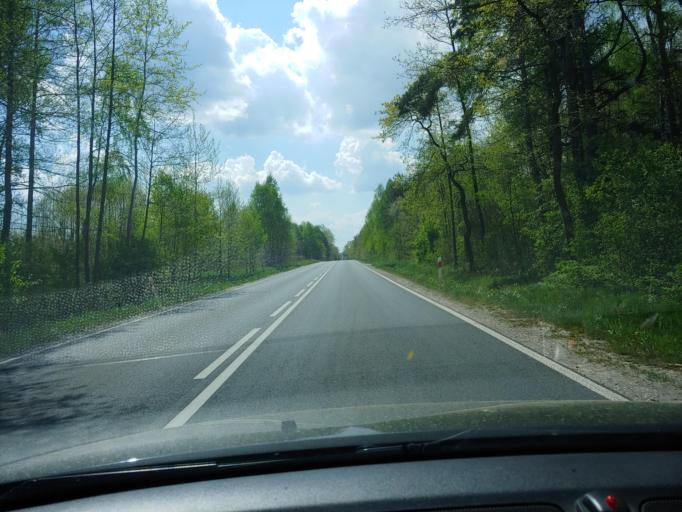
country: PL
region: Lesser Poland Voivodeship
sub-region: Powiat tarnowski
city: Lisia Gora
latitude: 50.1024
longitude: 21.0980
